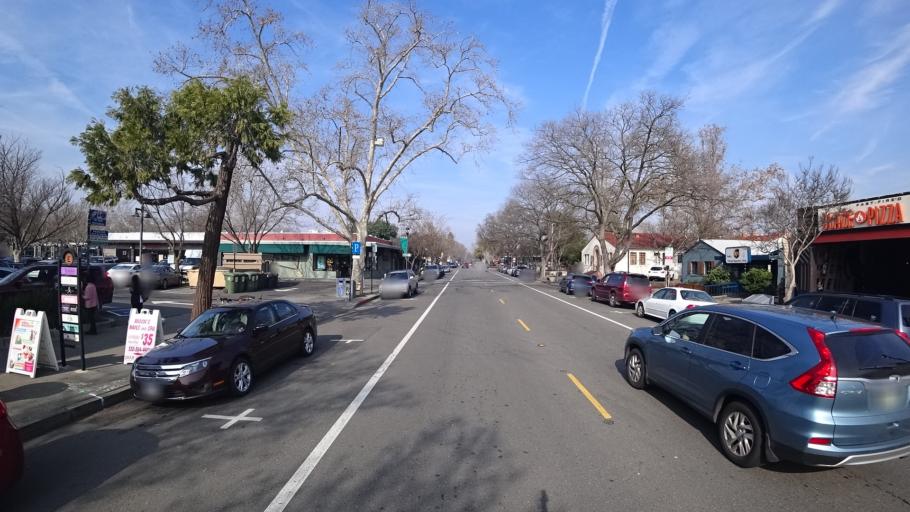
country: US
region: California
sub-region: Yolo County
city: Davis
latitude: 38.5439
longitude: -121.7402
